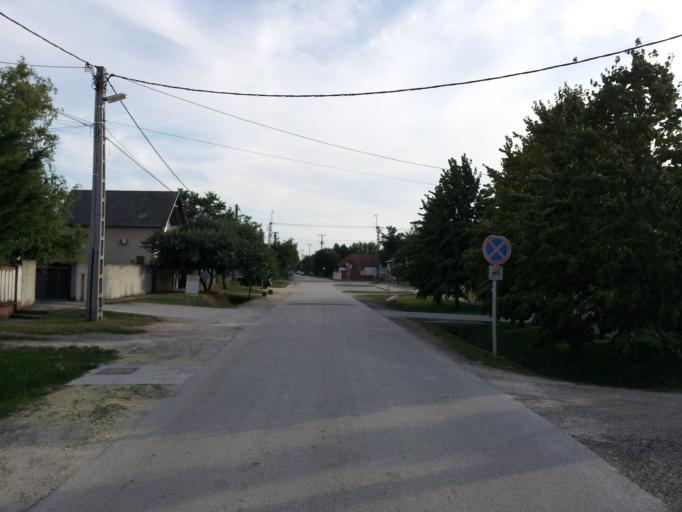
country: HU
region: Pest
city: Kiskunlachaza
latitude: 47.1900
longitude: 19.0103
